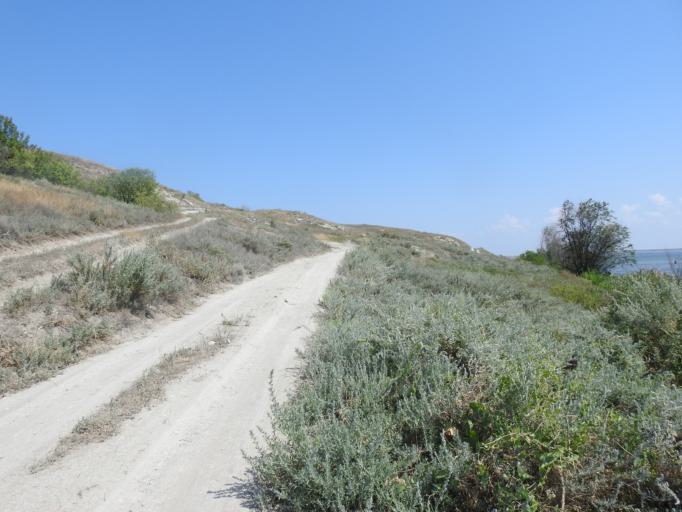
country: RU
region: Saratov
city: Kamenskiy
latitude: 50.5811
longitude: 45.7016
